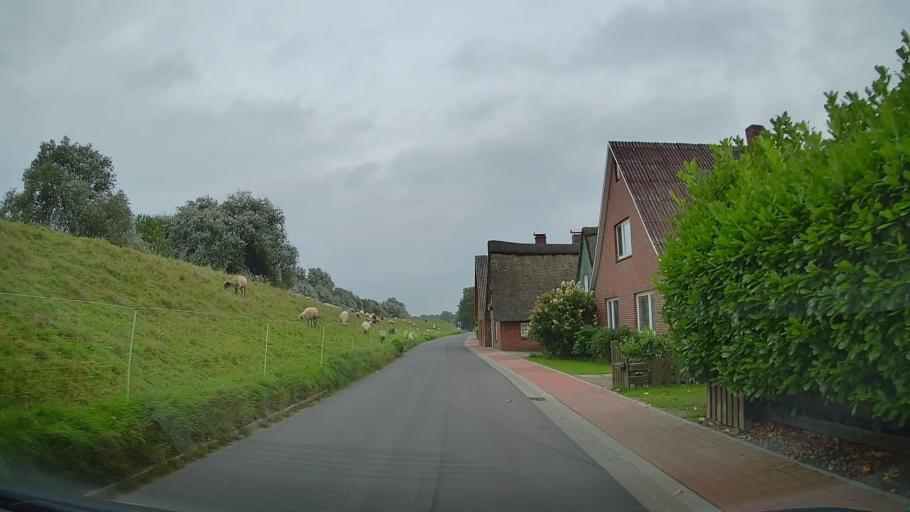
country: DE
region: Lower Saxony
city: Krummendeich
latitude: 53.8311
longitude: 9.2132
